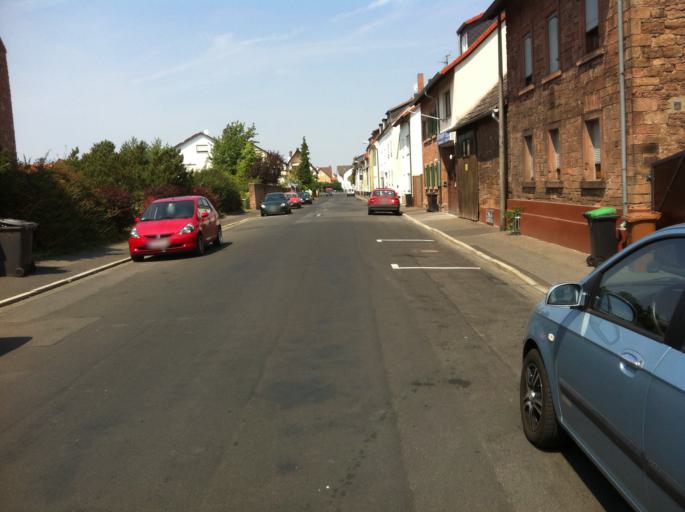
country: DE
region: Bavaria
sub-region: Regierungsbezirk Unterfranken
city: Niedernberg
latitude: 49.9344
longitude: 9.1335
